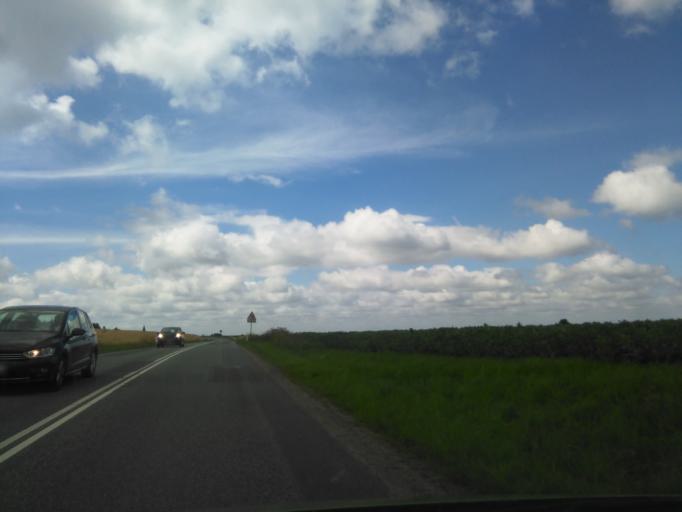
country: DK
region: Central Jutland
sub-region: Syddjurs Kommune
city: Ronde
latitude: 56.2519
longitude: 10.4999
